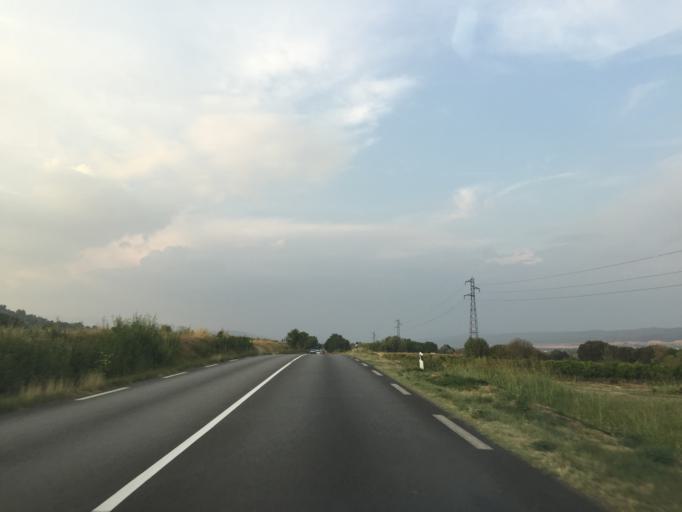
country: FR
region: Provence-Alpes-Cote d'Azur
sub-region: Departement des Alpes-de-Haute-Provence
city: Villeneuve
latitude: 43.8999
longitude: 5.8799
